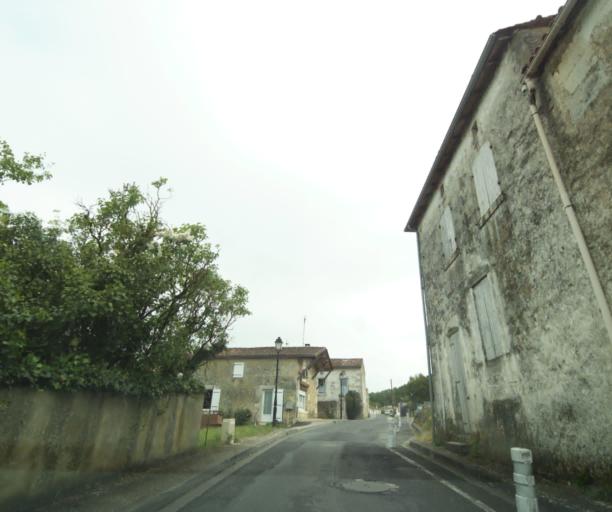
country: FR
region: Poitou-Charentes
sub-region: Departement de la Charente-Maritime
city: Chaniers
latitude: 45.7607
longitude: -0.5383
